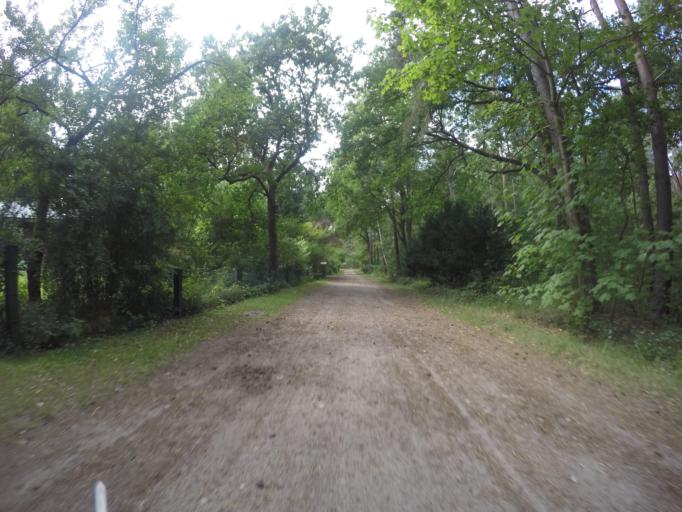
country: DE
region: Lower Saxony
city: Bleckede
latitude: 53.2774
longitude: 10.7335
